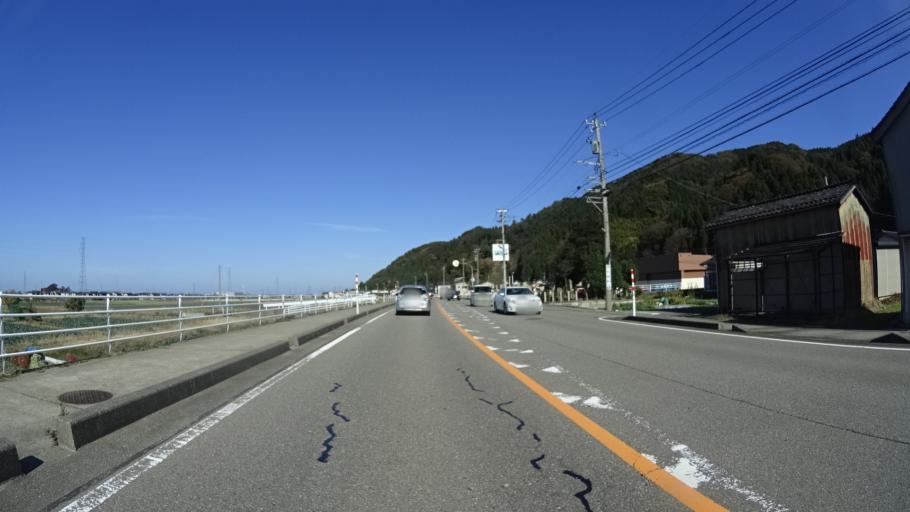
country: JP
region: Ishikawa
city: Tsurugi-asahimachi
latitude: 36.4614
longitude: 136.6208
